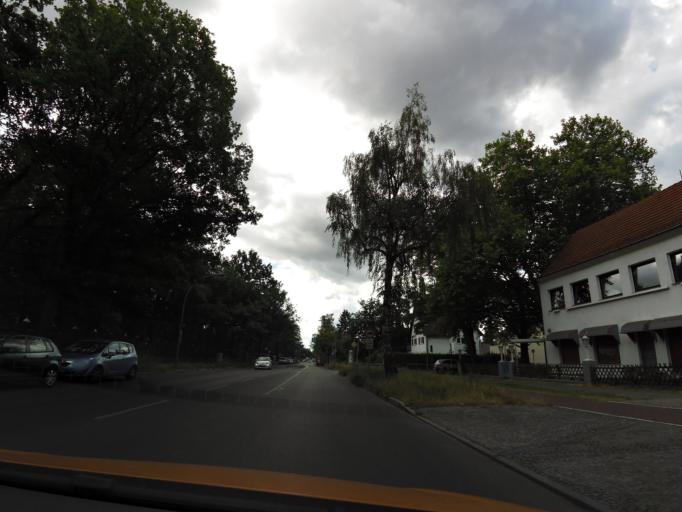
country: DE
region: Brandenburg
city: Teltow
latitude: 52.4172
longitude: 13.2654
